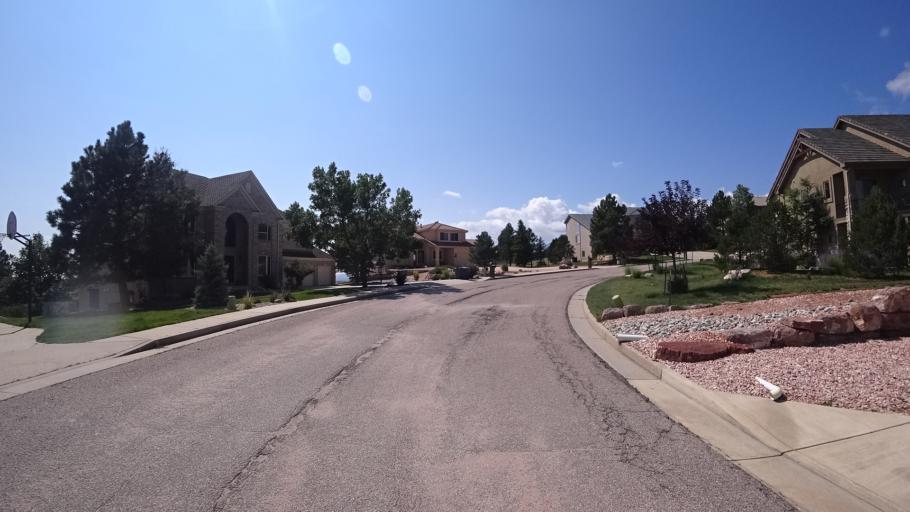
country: US
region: Colorado
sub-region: El Paso County
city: Manitou Springs
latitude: 38.9192
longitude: -104.8751
